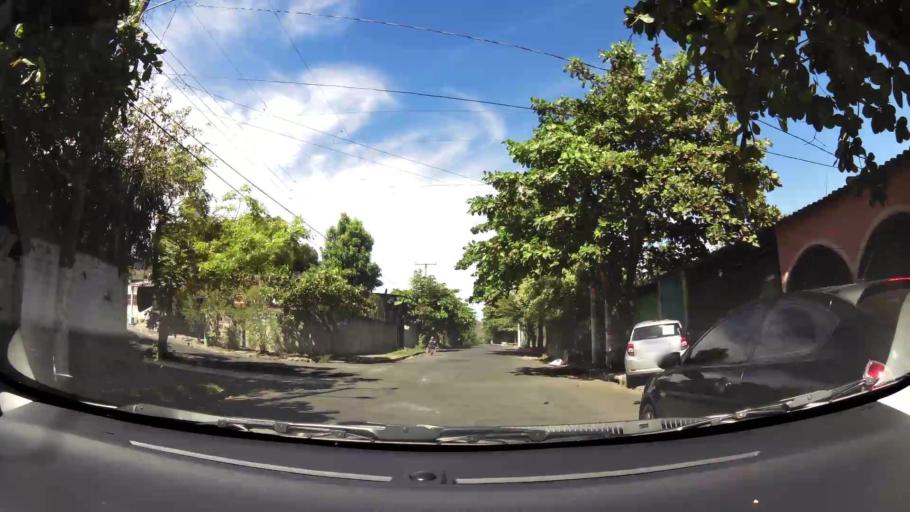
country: SV
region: San Salvador
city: Apopa
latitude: 13.8074
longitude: -89.1765
